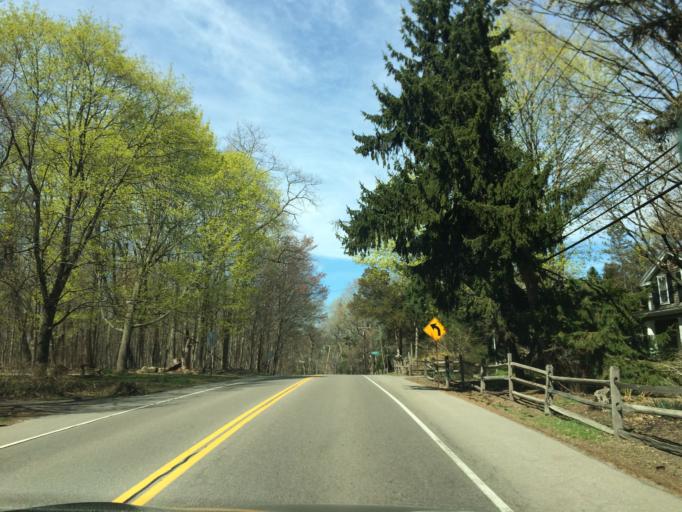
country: US
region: New York
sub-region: Monroe County
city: East Rochester
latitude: 43.0790
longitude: -77.4725
